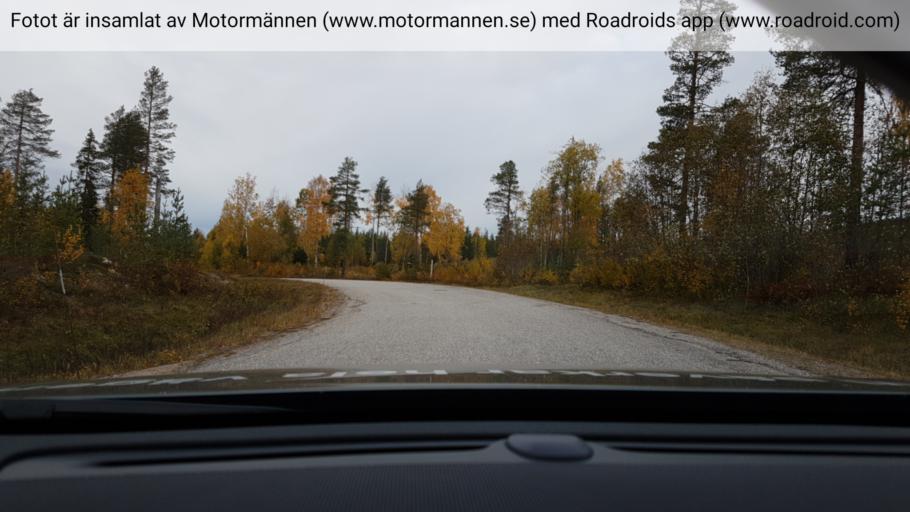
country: SE
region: Norrbotten
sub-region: Overkalix Kommun
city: OEverkalix
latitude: 66.2602
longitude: 23.0297
